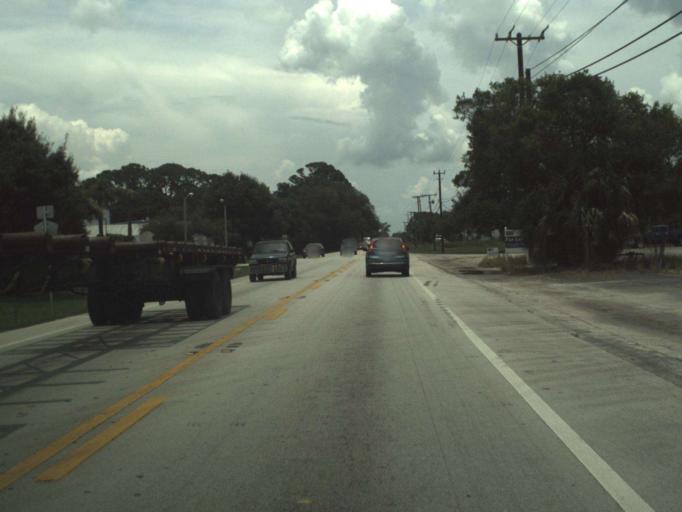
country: US
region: Florida
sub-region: Saint Lucie County
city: Lakewood Park
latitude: 27.4707
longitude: -80.3990
